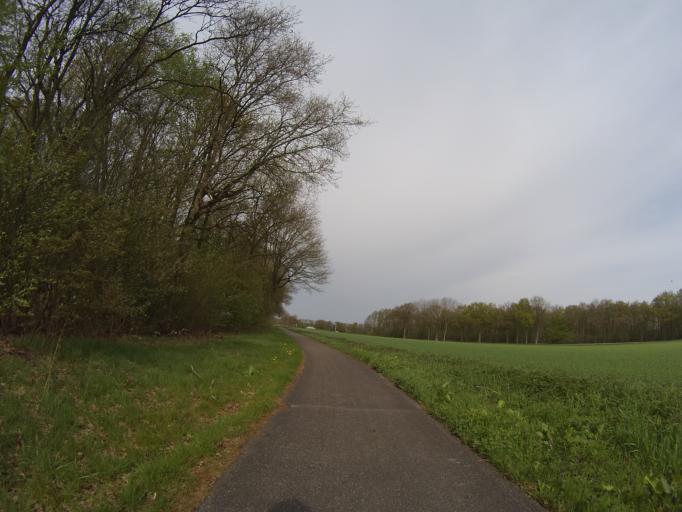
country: NL
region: Drenthe
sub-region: Gemeente Coevorden
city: Sleen
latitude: 52.8374
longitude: 6.6724
